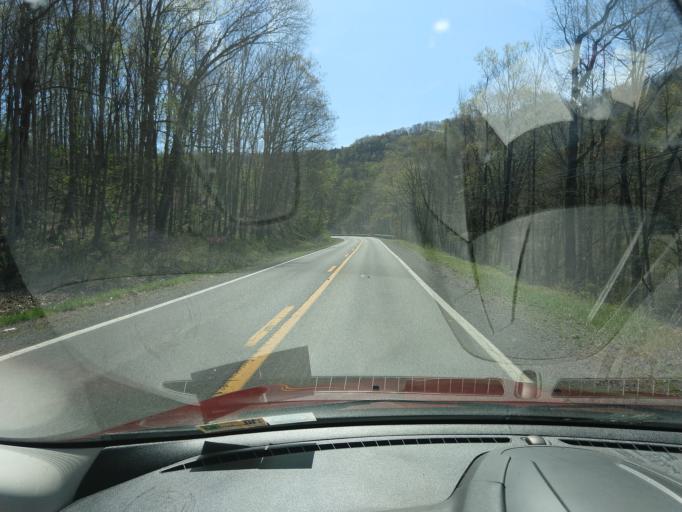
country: US
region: West Virginia
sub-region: Greenbrier County
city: Alderson
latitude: 37.7187
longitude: -80.6225
